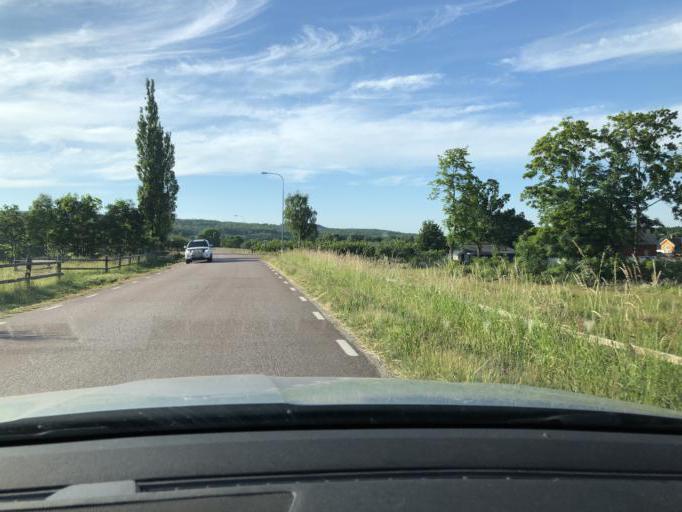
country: SE
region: Blekinge
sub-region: Solvesborgs Kommun
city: Soelvesborg
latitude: 56.1535
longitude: 14.6023
